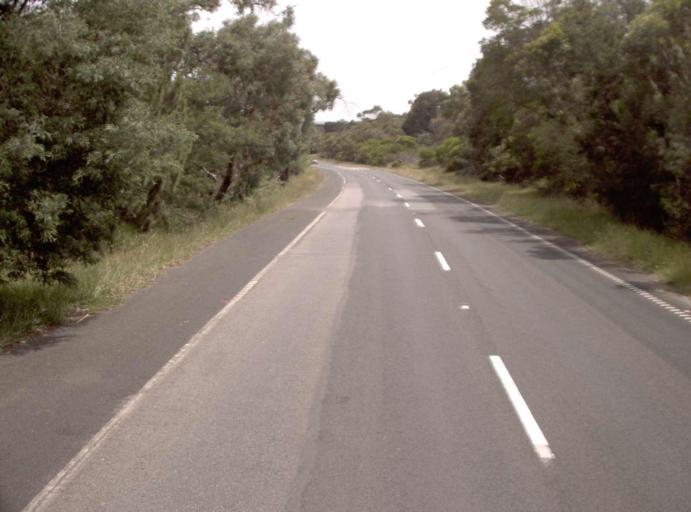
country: AU
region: Victoria
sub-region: Mornington Peninsula
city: Baxter
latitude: -38.1913
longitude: 145.1387
